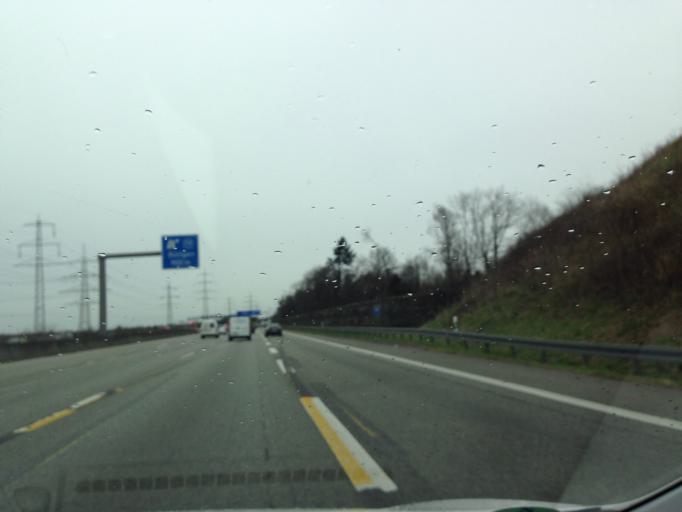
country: DE
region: North Rhine-Westphalia
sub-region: Regierungsbezirk Dusseldorf
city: Neuss
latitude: 51.1883
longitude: 6.6617
